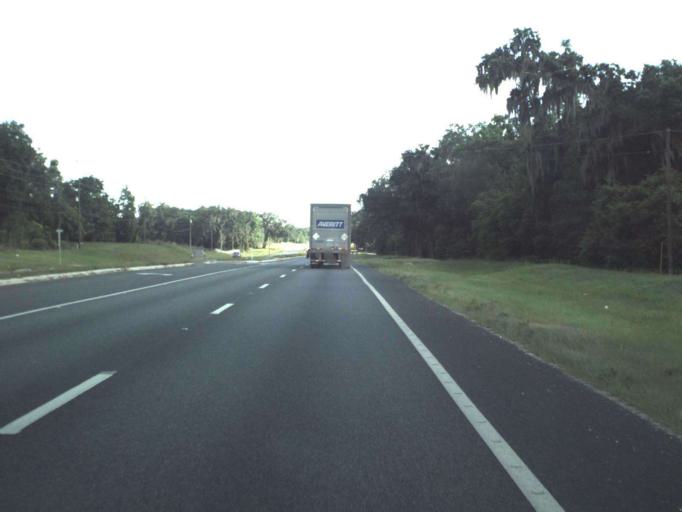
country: US
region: Florida
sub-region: Sumter County
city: Wildwood
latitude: 28.8961
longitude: -82.0371
